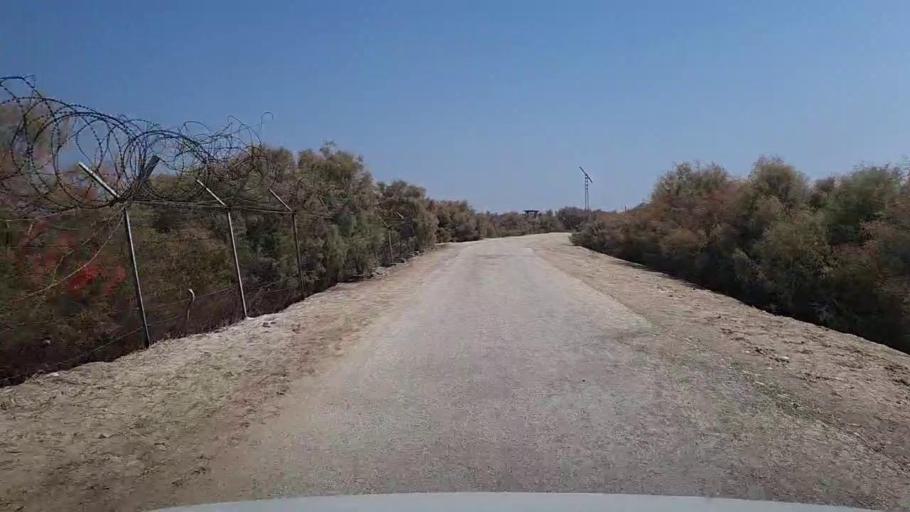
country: PK
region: Sindh
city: Kandhkot
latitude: 28.3014
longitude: 69.3507
